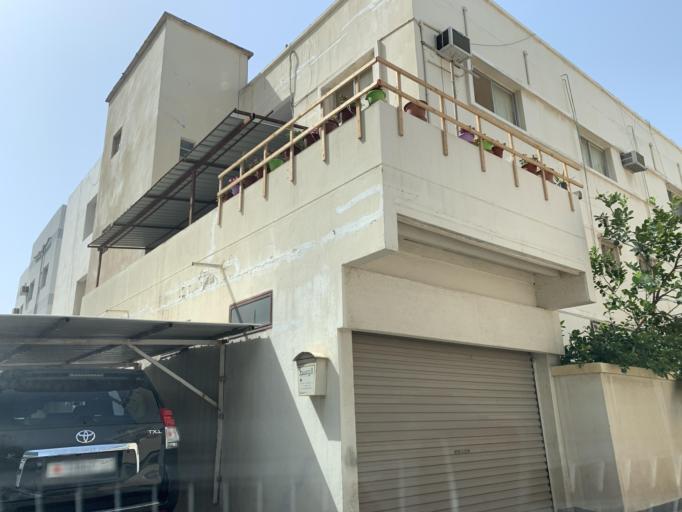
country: BH
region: Manama
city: Manama
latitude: 26.2098
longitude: 50.5870
